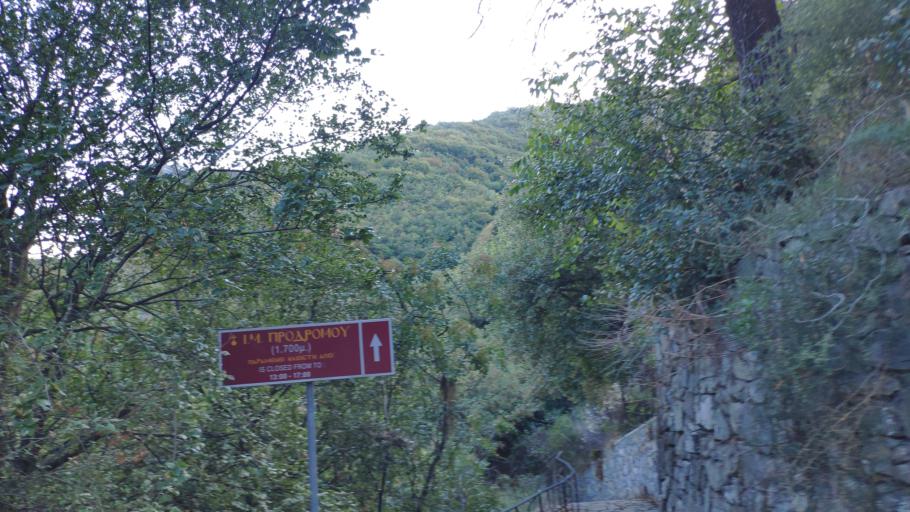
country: GR
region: Peloponnese
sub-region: Nomos Arkadias
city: Dimitsana
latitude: 37.5568
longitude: 22.0466
